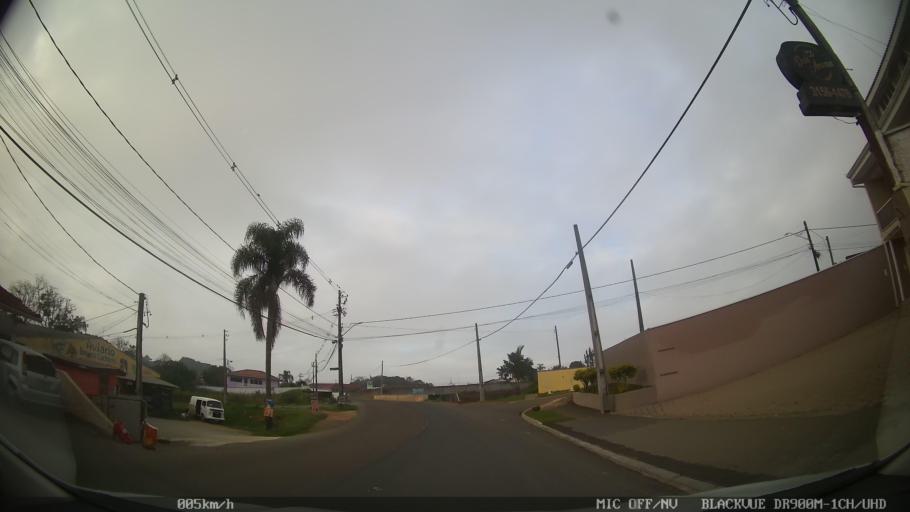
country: BR
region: Parana
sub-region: Almirante Tamandare
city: Almirante Tamandare
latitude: -25.3669
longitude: -49.3273
